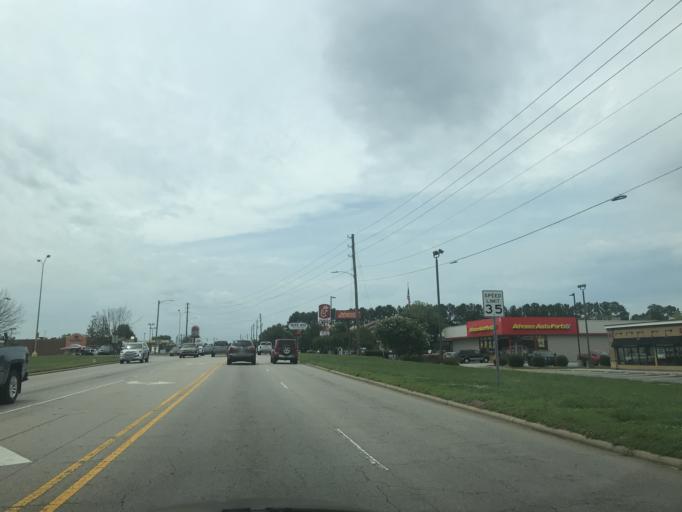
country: US
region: North Carolina
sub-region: Vance County
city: Henderson
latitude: 36.3350
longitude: -78.4380
